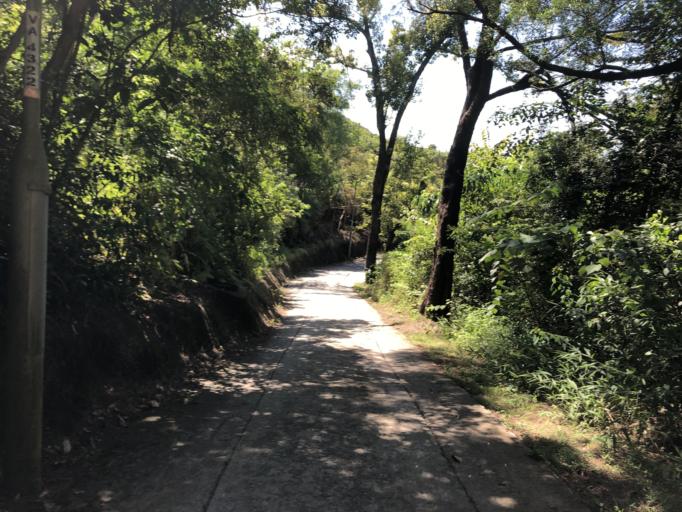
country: HK
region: Tuen Mun
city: Tuen Mun
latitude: 22.2942
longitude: 113.9735
